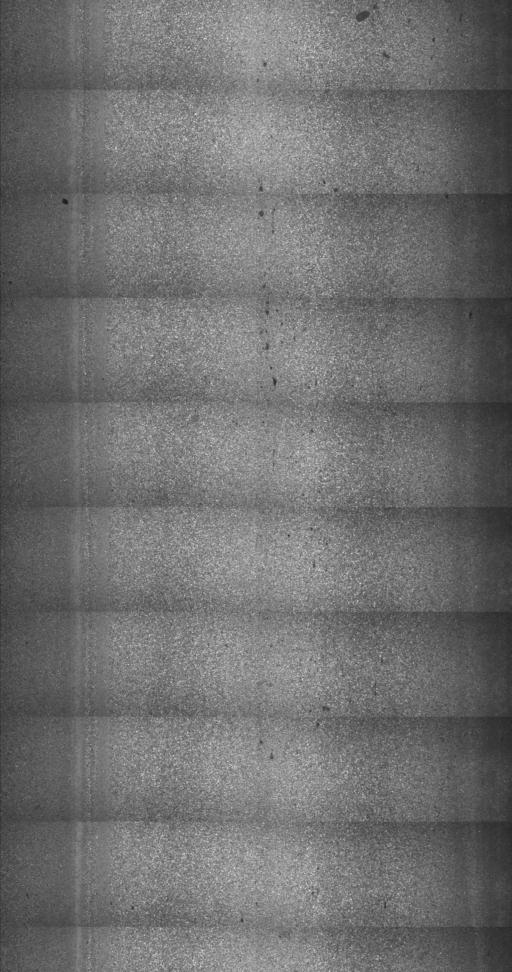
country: US
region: Vermont
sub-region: Chittenden County
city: Milton
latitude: 44.6820
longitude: -73.0372
